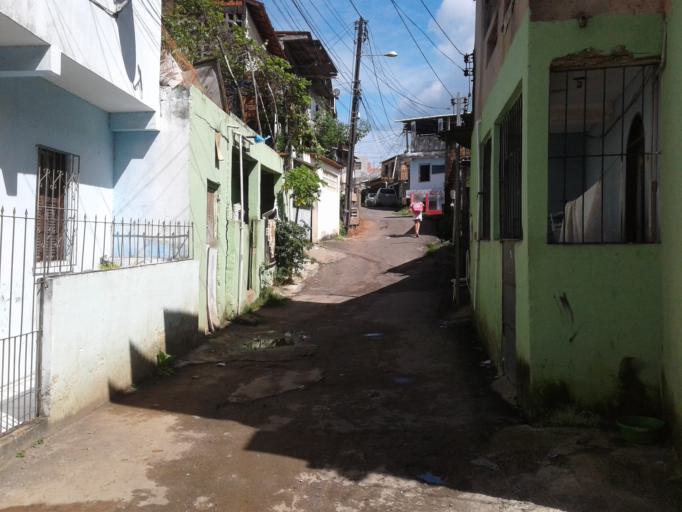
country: BR
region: Bahia
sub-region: Salvador
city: Salvador
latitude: -12.9113
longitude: -38.4671
